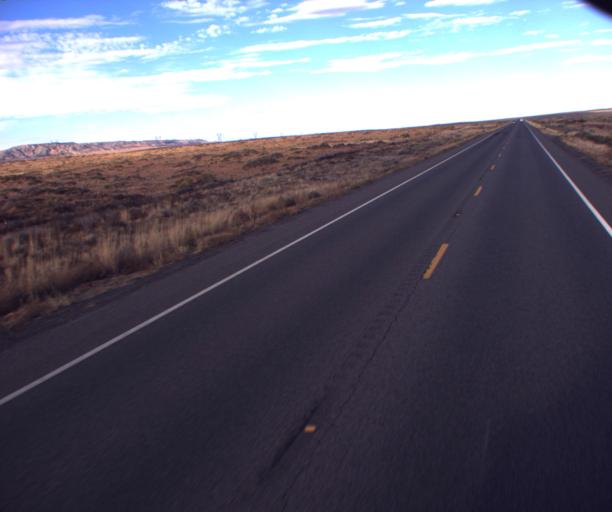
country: US
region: Arizona
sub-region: Apache County
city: Lukachukai
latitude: 36.9446
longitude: -109.2642
